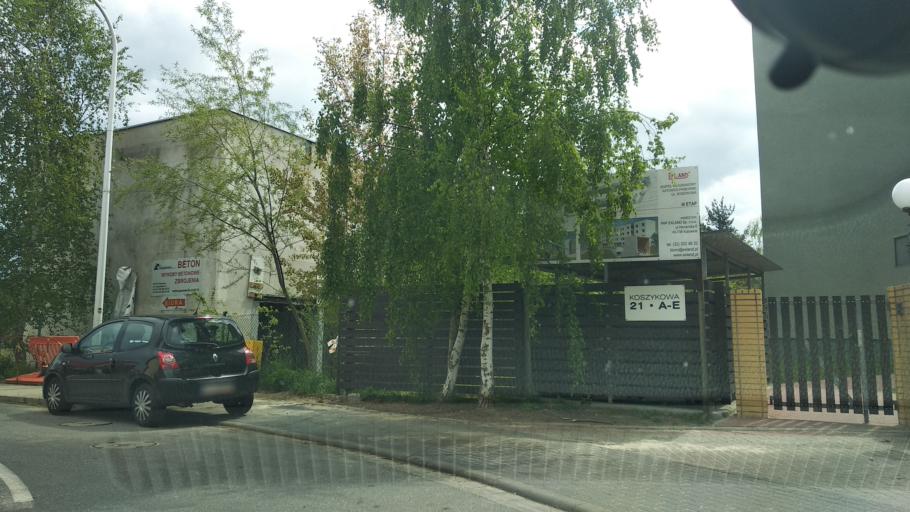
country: PL
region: Silesian Voivodeship
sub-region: Powiat mikolowski
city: Mikolow
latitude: 50.2248
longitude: 18.9209
